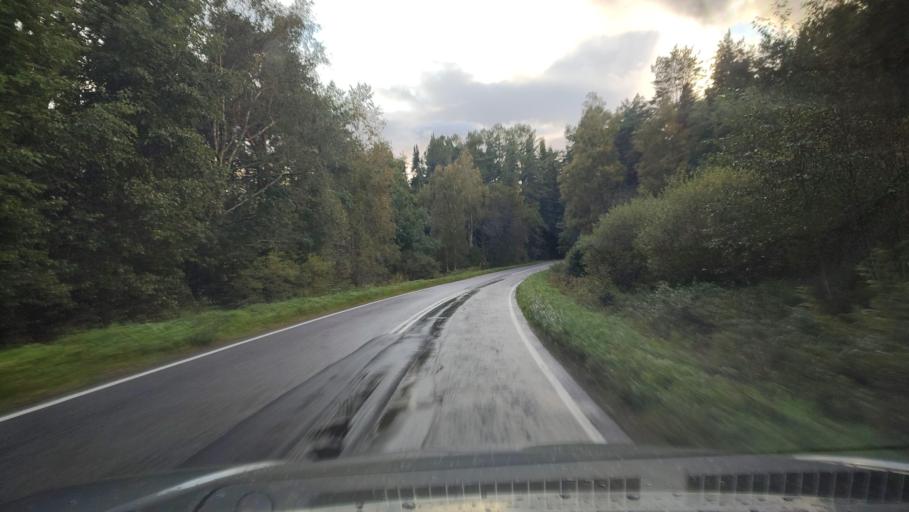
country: FI
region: Ostrobothnia
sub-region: Sydosterbotten
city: Kristinestad
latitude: 62.2814
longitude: 21.4165
